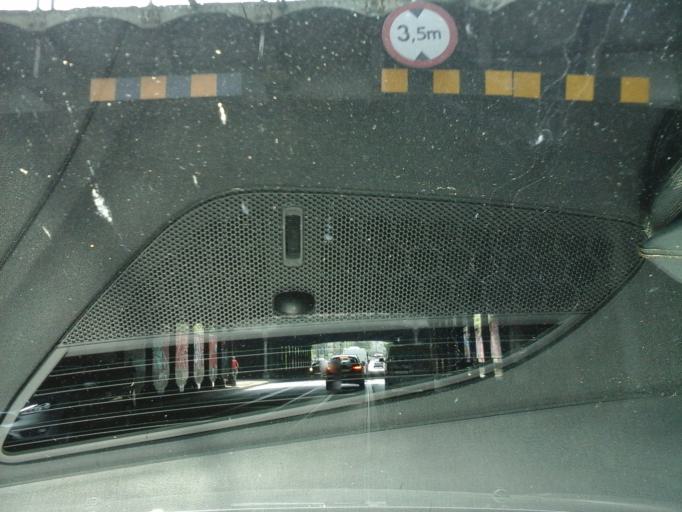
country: PL
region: Lower Silesian Voivodeship
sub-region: Powiat wroclawski
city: Wroclaw
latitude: 51.0976
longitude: 17.0429
